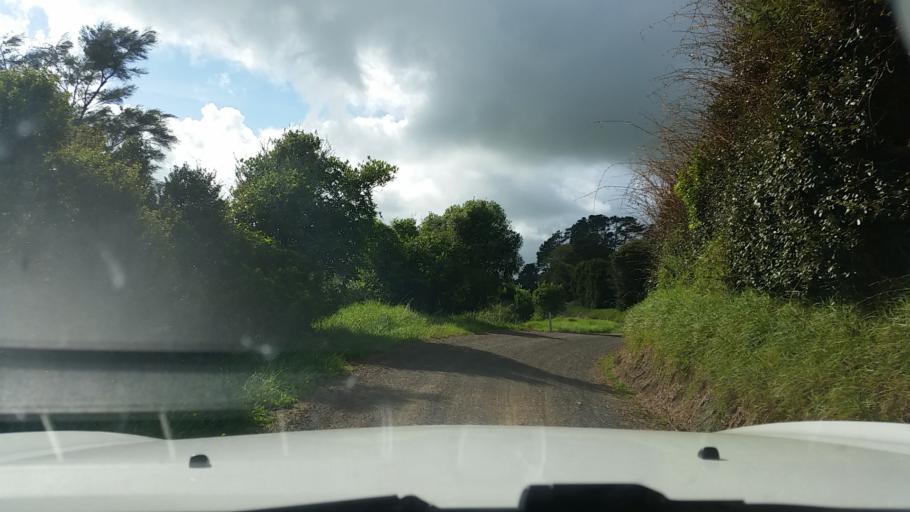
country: NZ
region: Waikato
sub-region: Hauraki District
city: Ngatea
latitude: -37.4640
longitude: 175.4646
